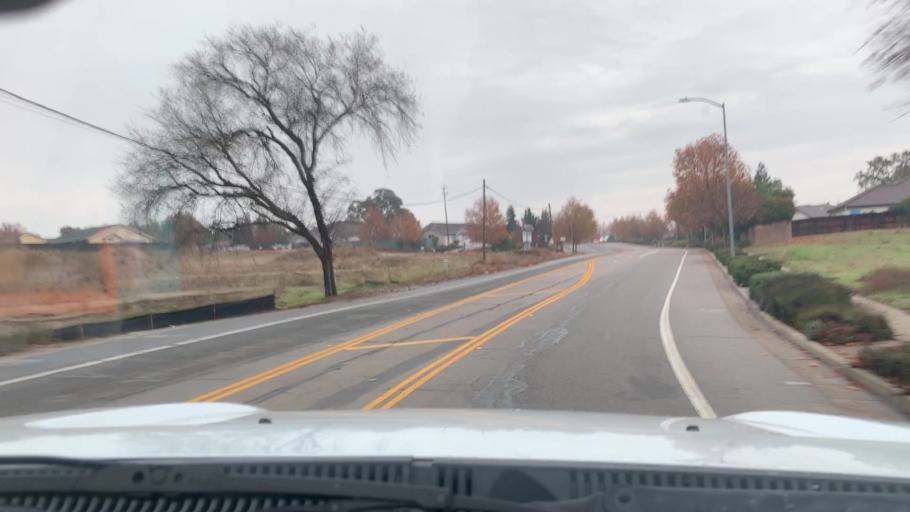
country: US
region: California
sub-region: San Luis Obispo County
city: Paso Robles
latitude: 35.6382
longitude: -120.6621
